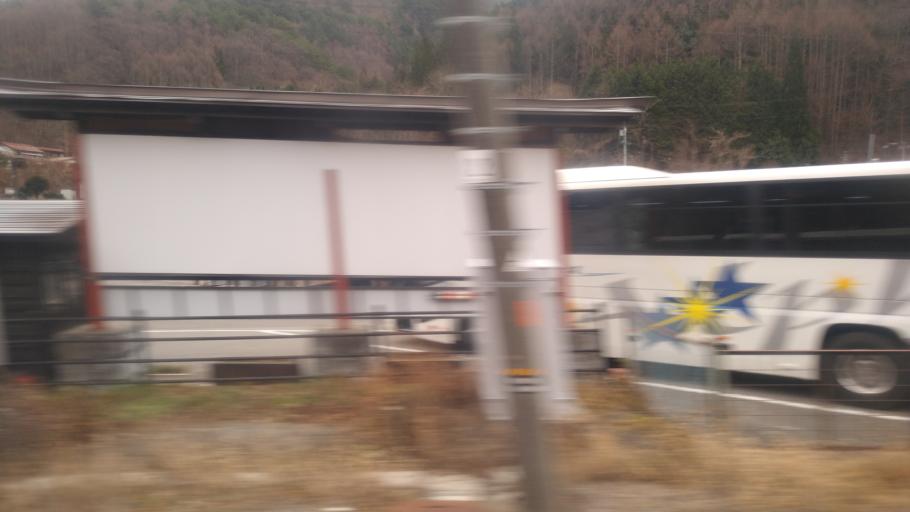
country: JP
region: Nagano
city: Tatsuno
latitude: 35.9624
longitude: 137.8092
